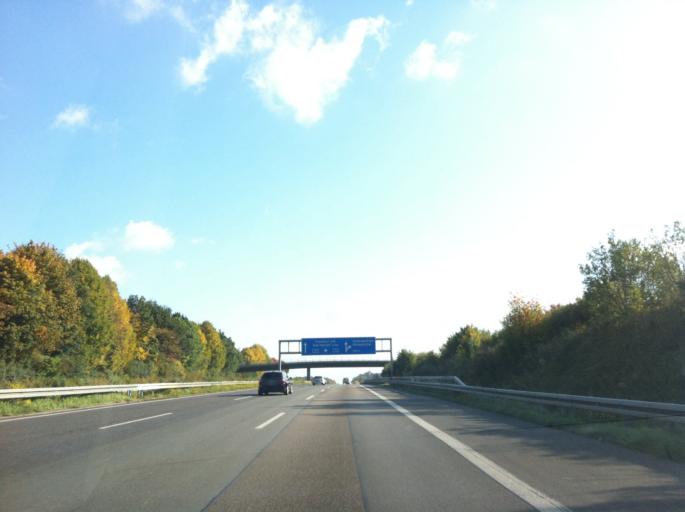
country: DE
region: North Rhine-Westphalia
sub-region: Regierungsbezirk Koln
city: Bad Honnef
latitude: 50.6972
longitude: 7.2634
